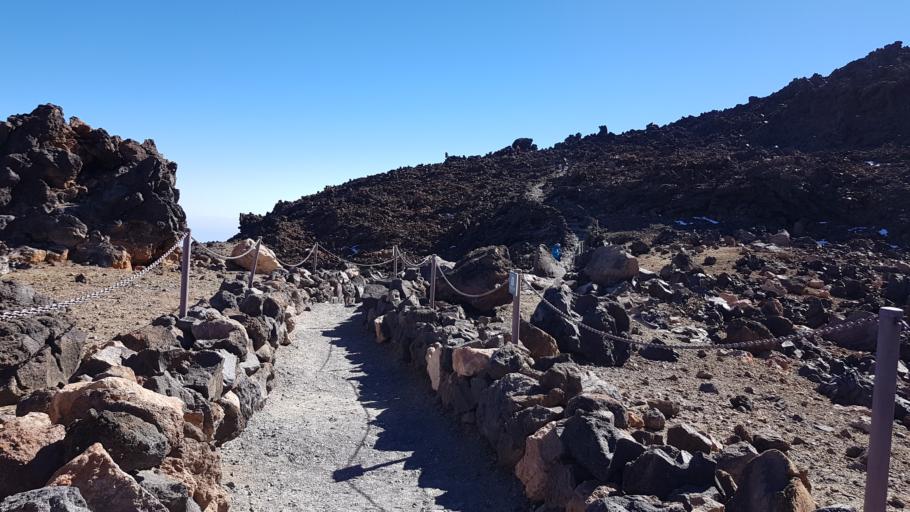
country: ES
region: Canary Islands
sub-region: Provincia de Santa Cruz de Tenerife
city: La Guancha
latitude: 28.2740
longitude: -16.6391
